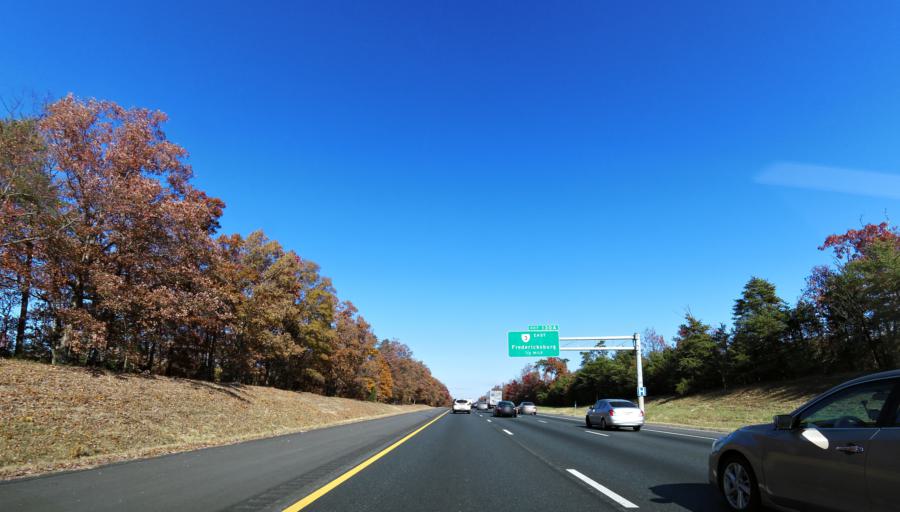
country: US
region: Virginia
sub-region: City of Fredericksburg
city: Fredericksburg
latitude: 38.2836
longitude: -77.5097
